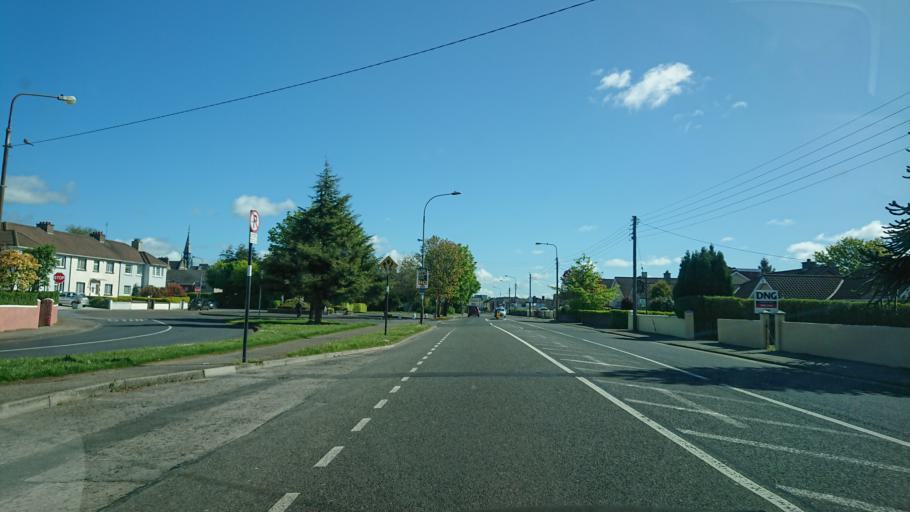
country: IE
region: Munster
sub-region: Waterford
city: Waterford
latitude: 52.2499
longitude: -7.1204
